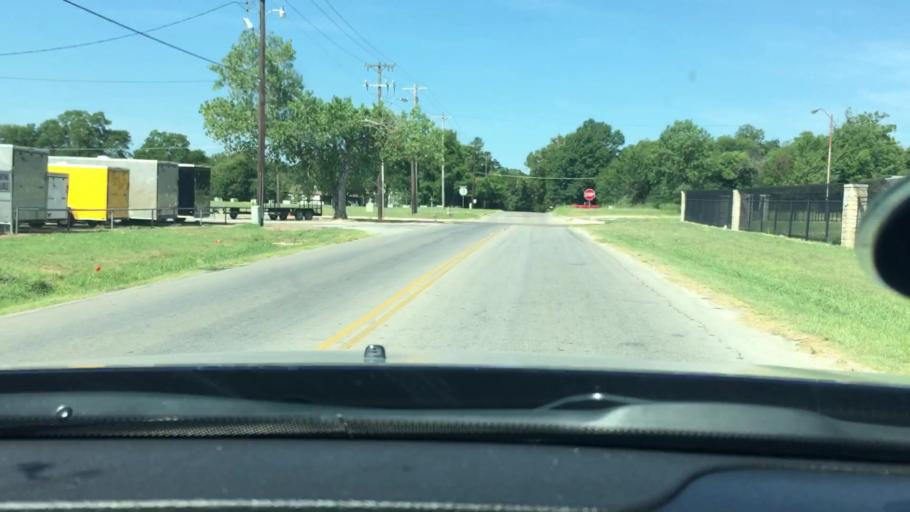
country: US
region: Oklahoma
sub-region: Carter County
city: Ardmore
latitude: 34.1585
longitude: -97.1204
